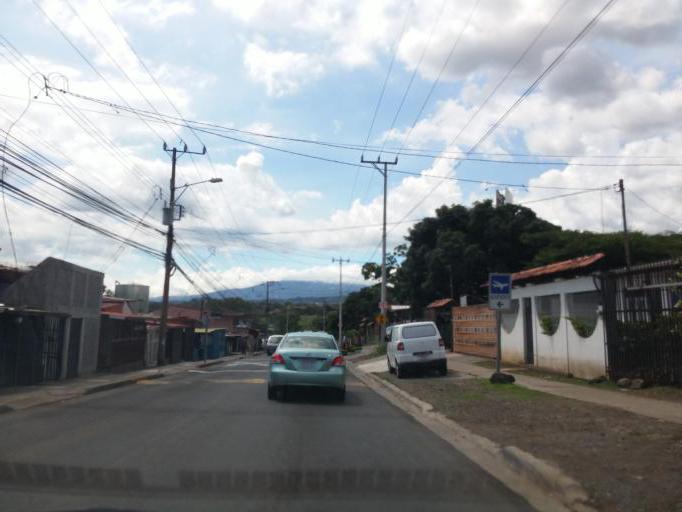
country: CR
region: Heredia
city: Llorente
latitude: 10.0029
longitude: -84.1709
